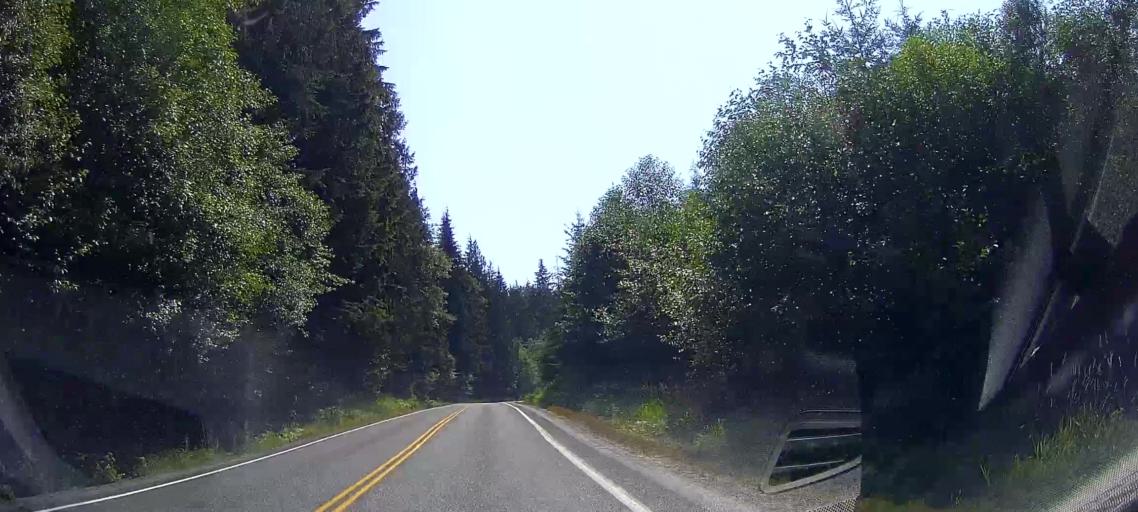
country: US
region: Washington
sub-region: Snohomish County
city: Bryant
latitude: 48.3418
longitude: -122.1089
